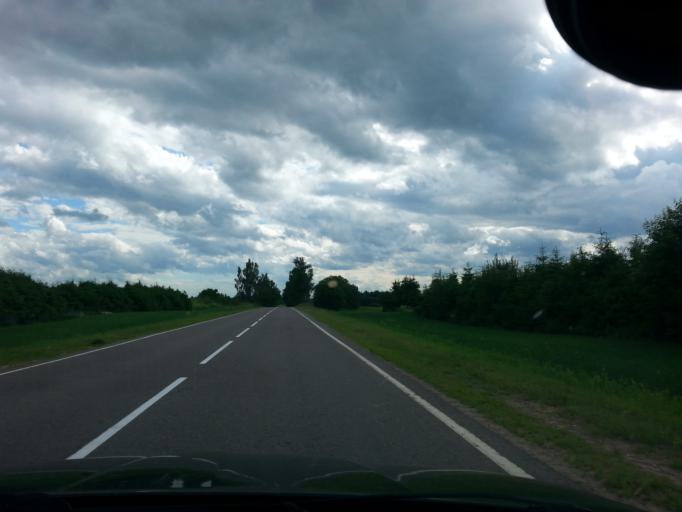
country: BY
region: Minsk
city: Svir
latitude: 54.9098
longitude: 26.3936
